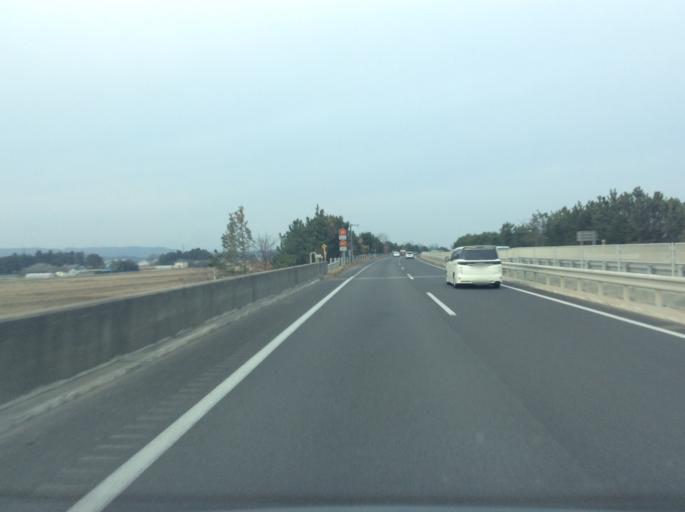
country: JP
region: Miyagi
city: Iwanuma
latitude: 38.1188
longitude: 140.8869
